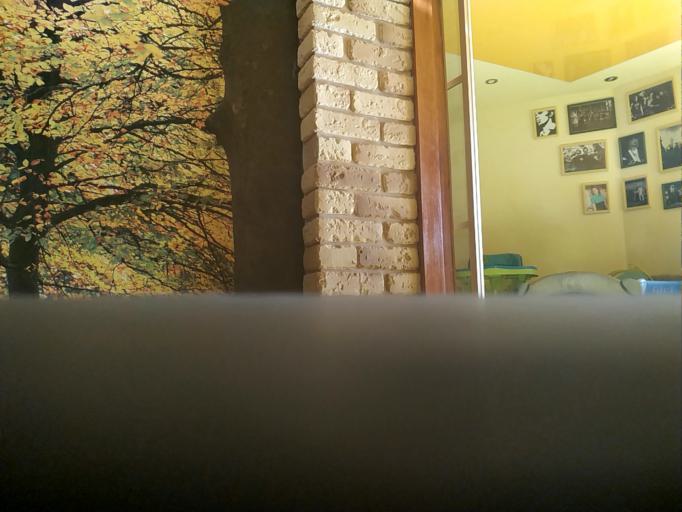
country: RU
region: Smolensk
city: Temkino
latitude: 55.0819
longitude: 34.9066
